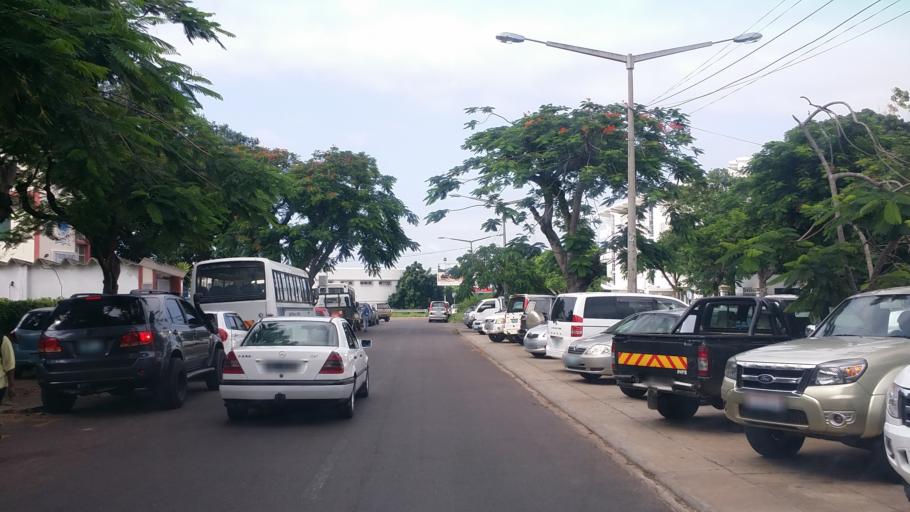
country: MZ
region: Maputo City
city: Maputo
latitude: -25.9796
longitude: 32.5922
